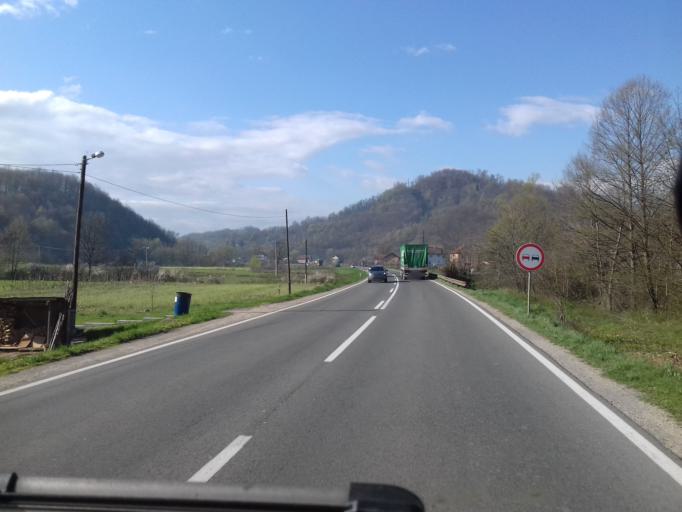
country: BA
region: Federation of Bosnia and Herzegovina
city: Lijesnica
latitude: 44.5166
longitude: 18.0827
